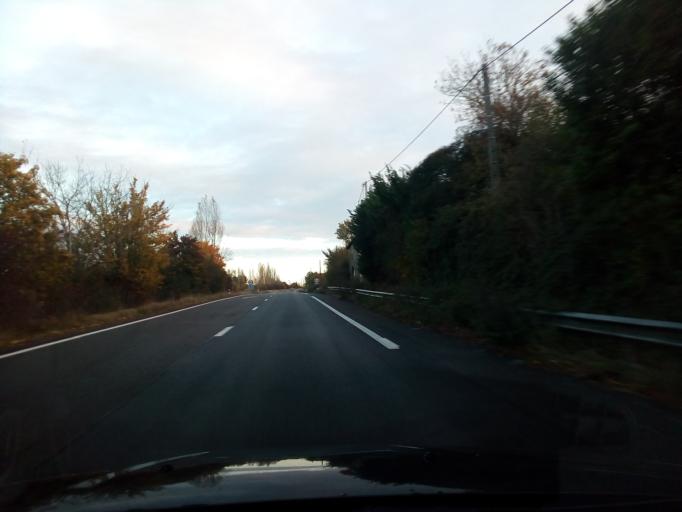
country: FR
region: Poitou-Charentes
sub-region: Departement de la Charente-Maritime
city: Chevanceaux
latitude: 45.3186
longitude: -0.2295
